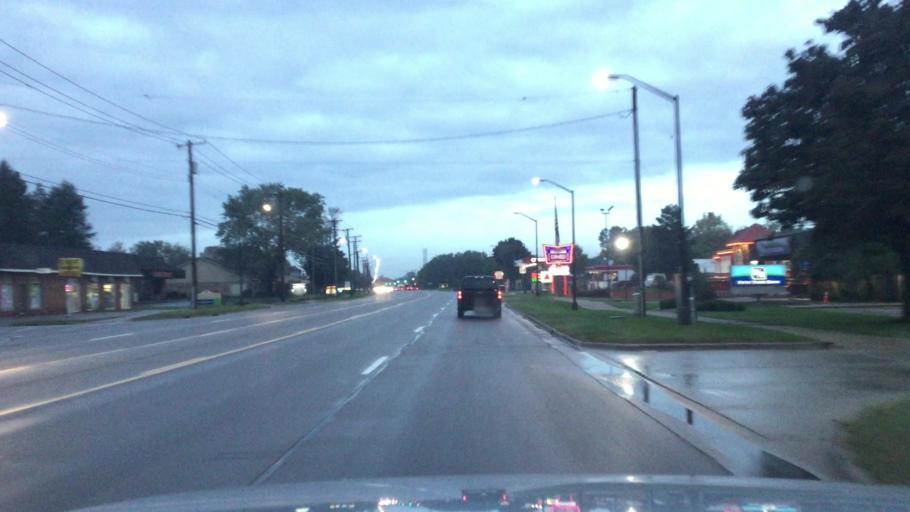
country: US
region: Michigan
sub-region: Oakland County
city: Waterford
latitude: 42.7140
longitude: -83.4109
